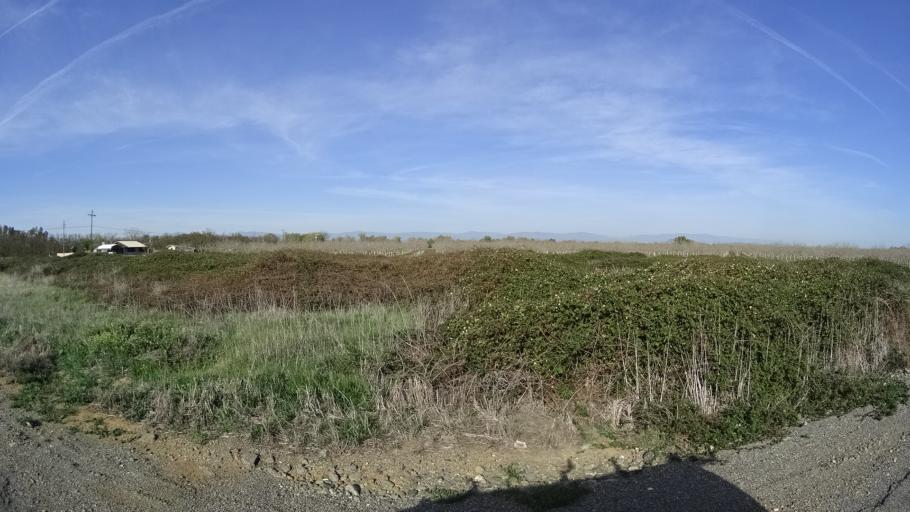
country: US
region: California
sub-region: Glenn County
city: Orland
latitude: 39.6979
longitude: -122.2154
